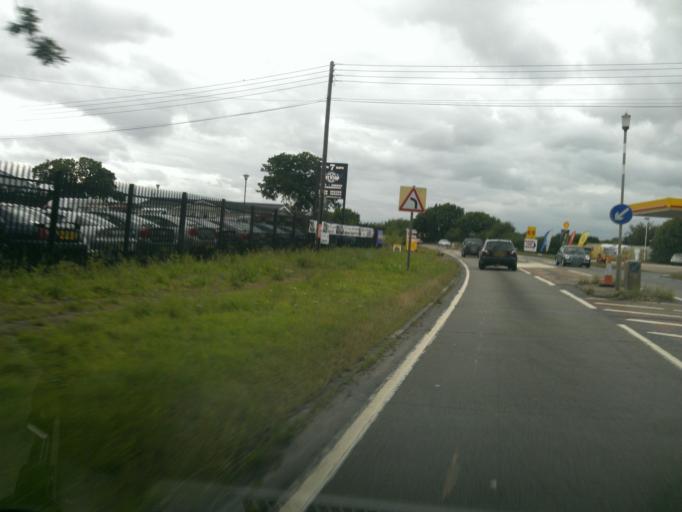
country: GB
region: England
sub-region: Essex
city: Great Bentley
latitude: 51.8679
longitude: 1.0750
